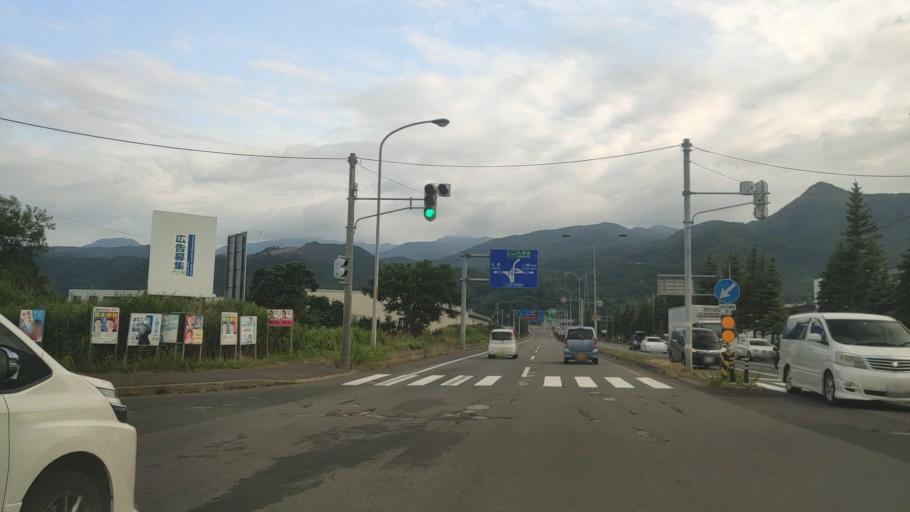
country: JP
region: Hokkaido
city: Otaru
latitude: 43.1415
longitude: 141.1794
